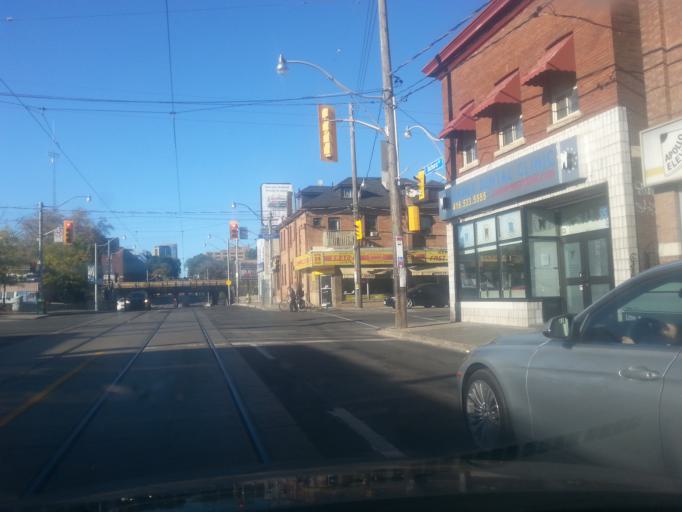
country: CA
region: Ontario
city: Toronto
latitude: 43.6729
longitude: -79.4143
